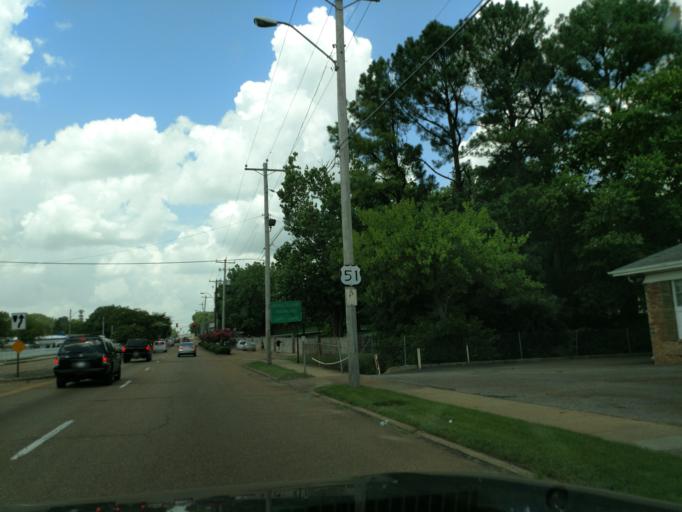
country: US
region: Tennessee
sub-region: Shelby County
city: New South Memphis
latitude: 35.0448
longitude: -90.0250
